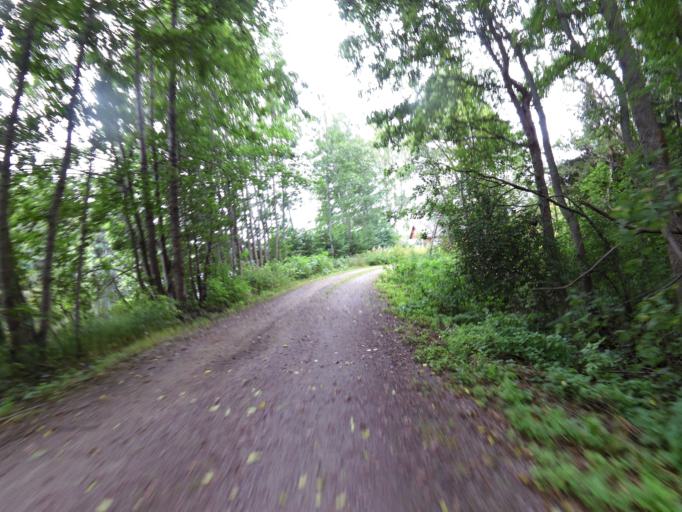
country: SE
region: Gaevleborg
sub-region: Gavle Kommun
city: Valbo
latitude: 60.7541
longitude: 16.9718
